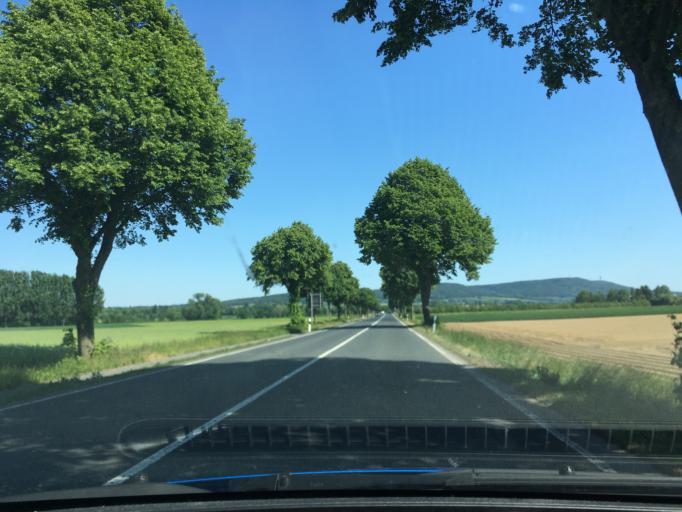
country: DE
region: Lower Saxony
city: Rodenberg
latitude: 52.3295
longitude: 9.3411
